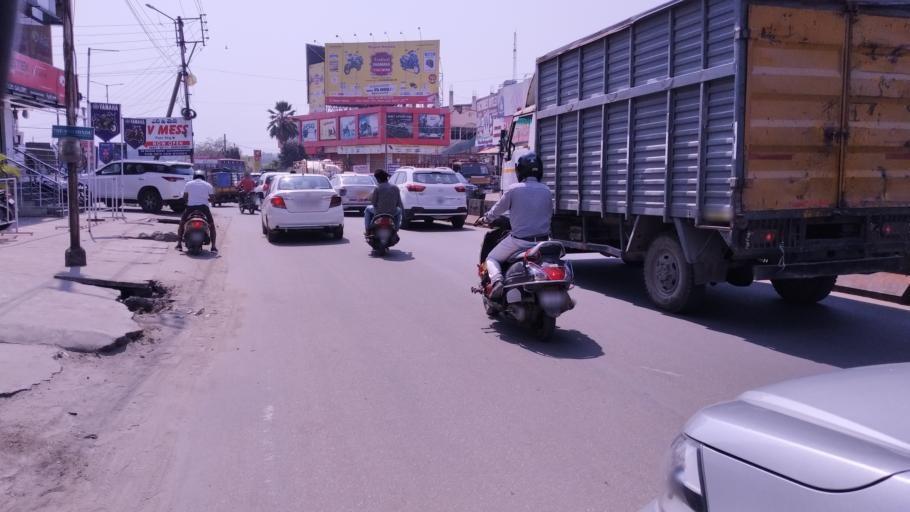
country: IN
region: Telangana
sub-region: Hyderabad
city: Malkajgiri
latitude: 17.4563
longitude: 78.4851
